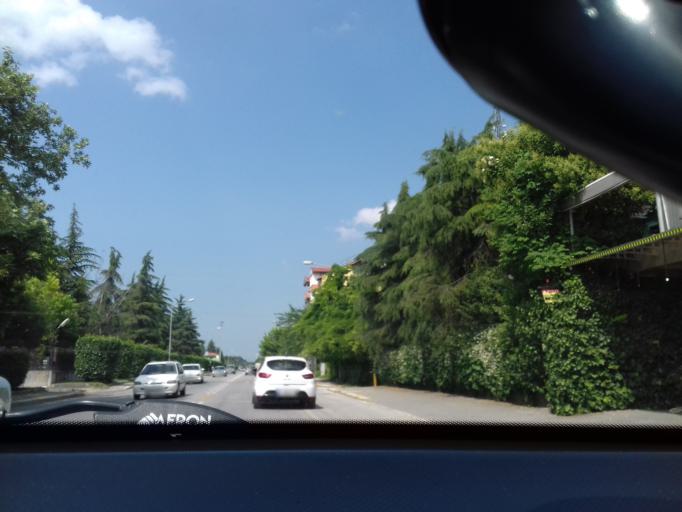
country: TR
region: Sakarya
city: Adapazari
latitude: 40.7209
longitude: 30.3691
